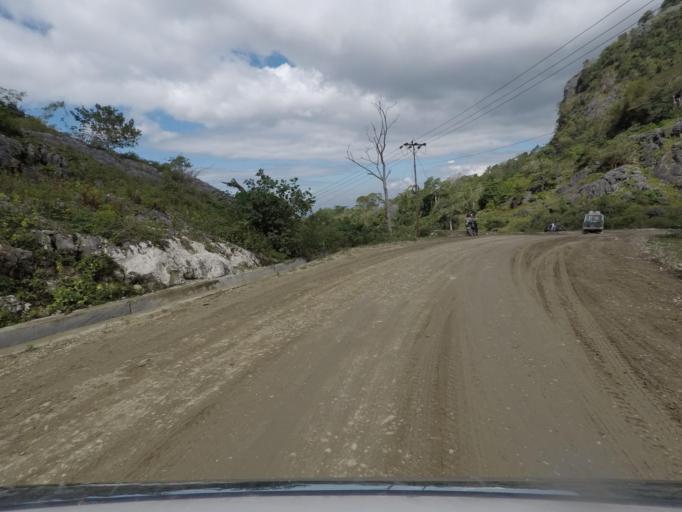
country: TL
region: Baucau
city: Venilale
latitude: -8.7303
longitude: 126.3686
